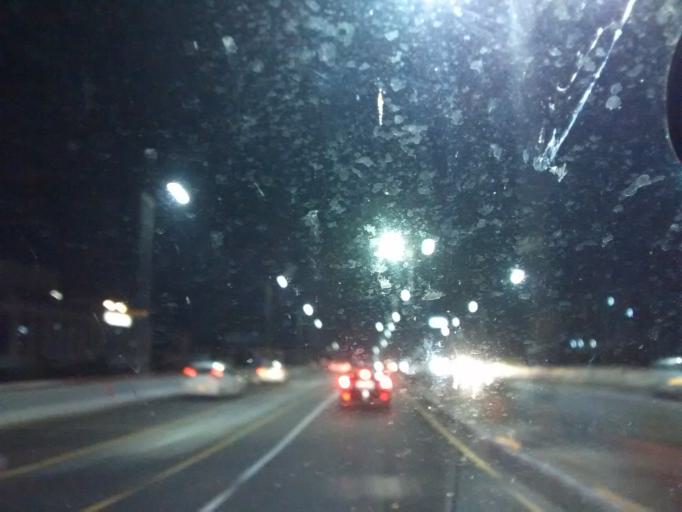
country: IN
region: Telangana
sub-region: Hyderabad
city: Hyderabad
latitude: 17.3466
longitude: 78.4160
